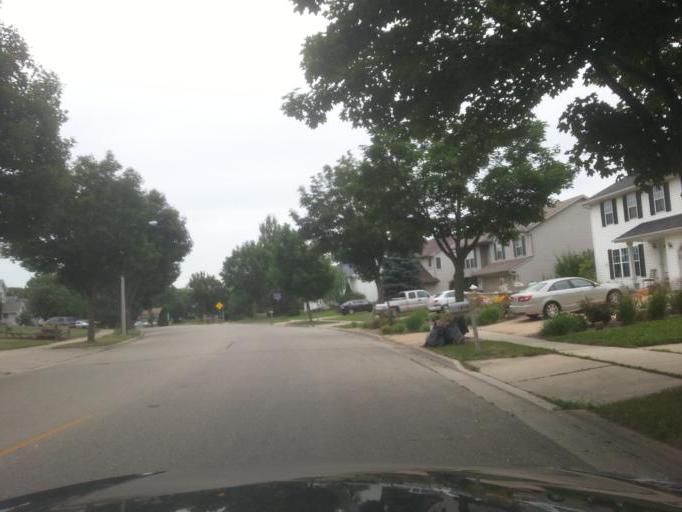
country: US
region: Wisconsin
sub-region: Dane County
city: Monona
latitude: 43.0732
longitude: -89.2829
